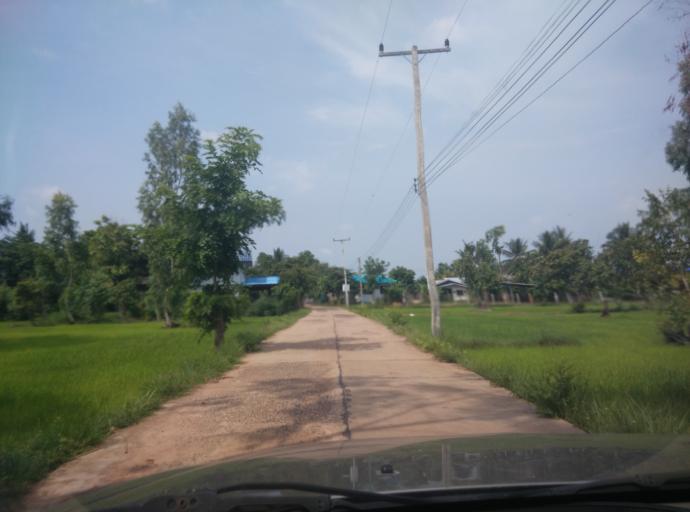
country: TH
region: Sisaket
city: Huai Thap Than
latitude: 15.0481
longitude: 104.0819
